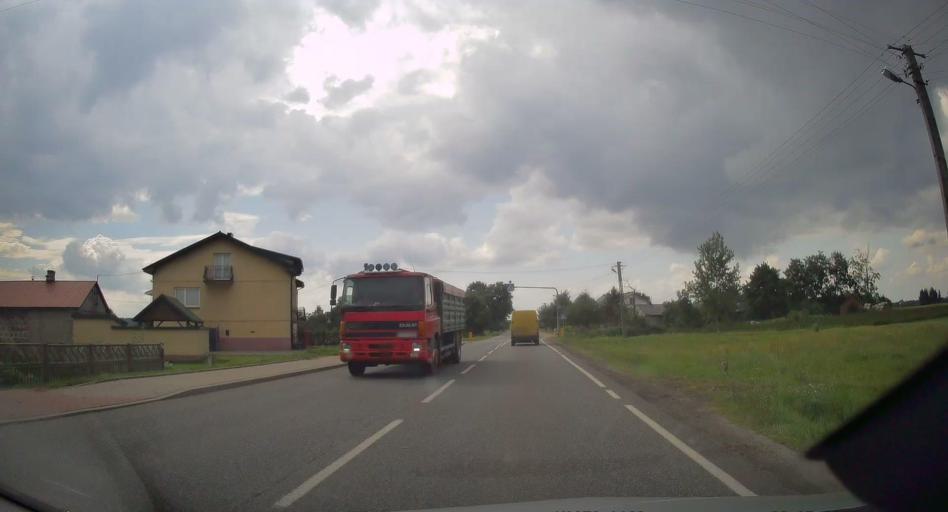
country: PL
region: Lodz Voivodeship
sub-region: Powiat skierniewicki
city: Gluchow
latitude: 51.7725
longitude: 20.1404
